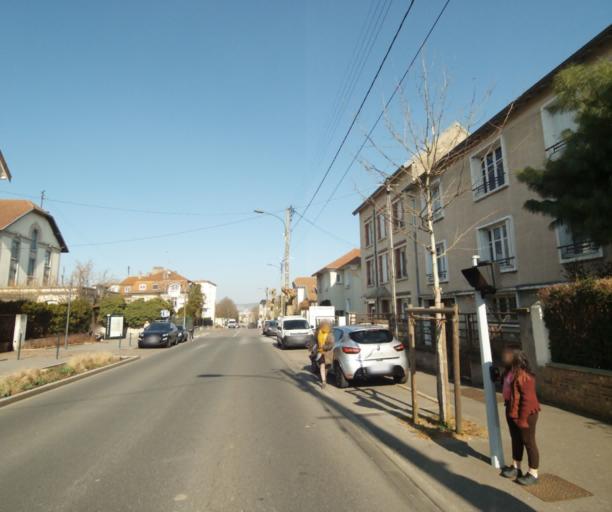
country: FR
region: Lorraine
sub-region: Departement de Meurthe-et-Moselle
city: Jarville-la-Malgrange
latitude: 48.6682
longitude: 6.1990
